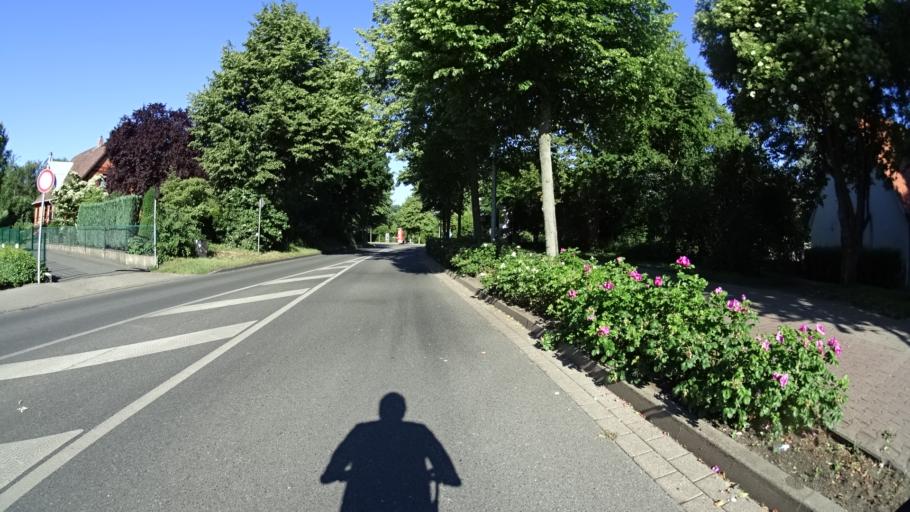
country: DE
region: Lower Saxony
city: Lueneburg
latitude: 53.2457
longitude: 10.4006
